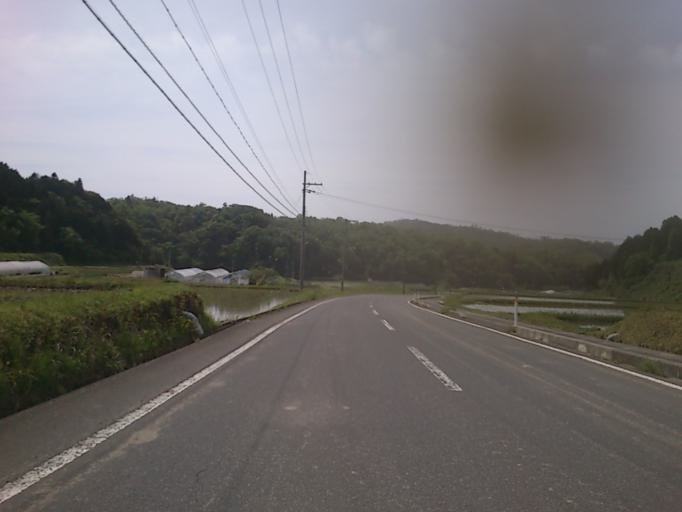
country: JP
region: Kyoto
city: Miyazu
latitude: 35.6056
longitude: 135.1470
